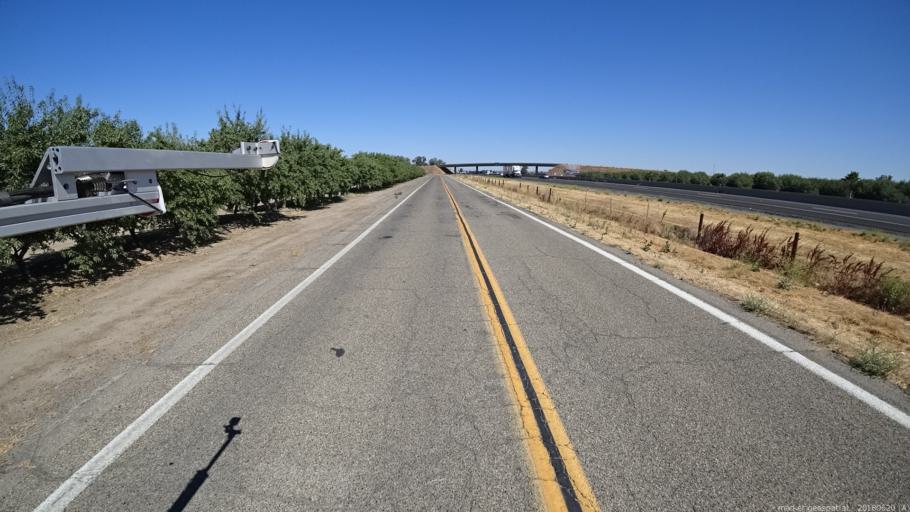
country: US
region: California
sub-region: Madera County
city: Parkwood
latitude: 36.9359
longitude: -120.0342
